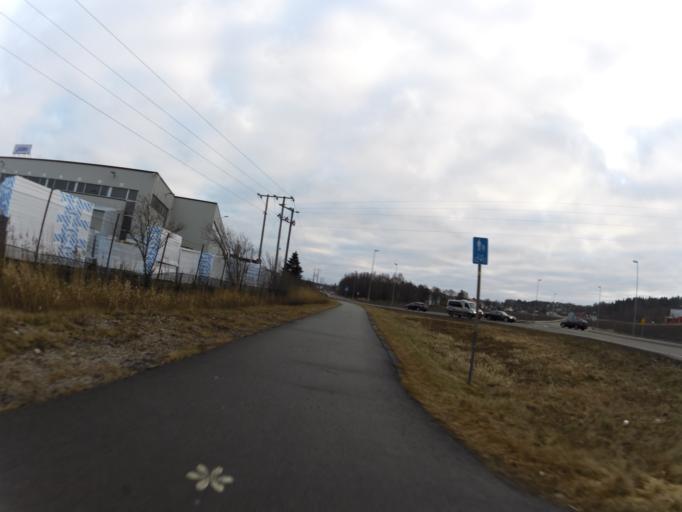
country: NO
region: Ostfold
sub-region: Fredrikstad
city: Fredrikstad
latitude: 59.2079
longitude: 10.8882
